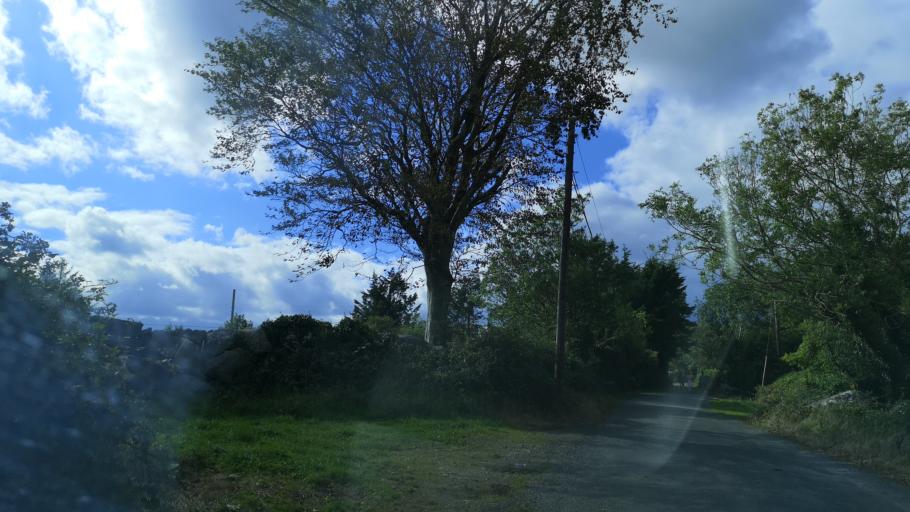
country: IE
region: Connaught
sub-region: County Galway
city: Moycullen
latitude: 53.3547
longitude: -9.1629
